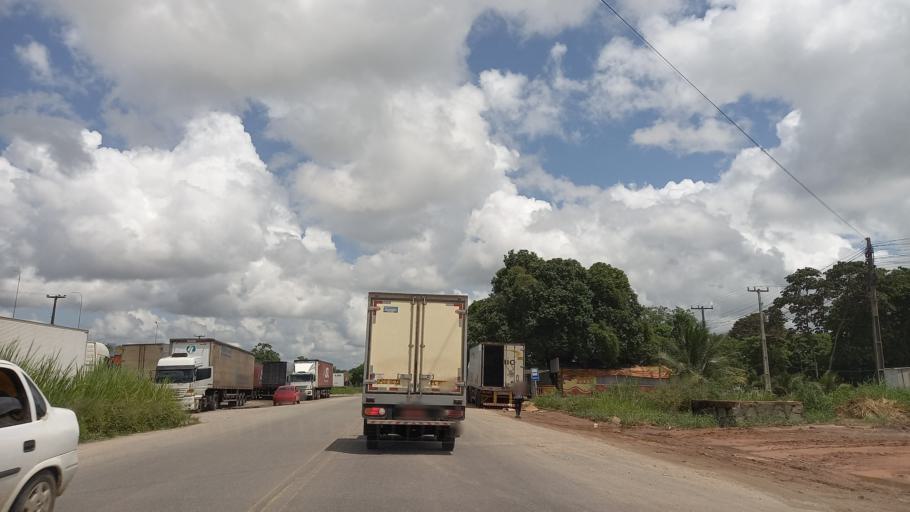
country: BR
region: Pernambuco
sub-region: Cabo De Santo Agostinho
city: Cabo
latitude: -8.2478
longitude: -34.9997
